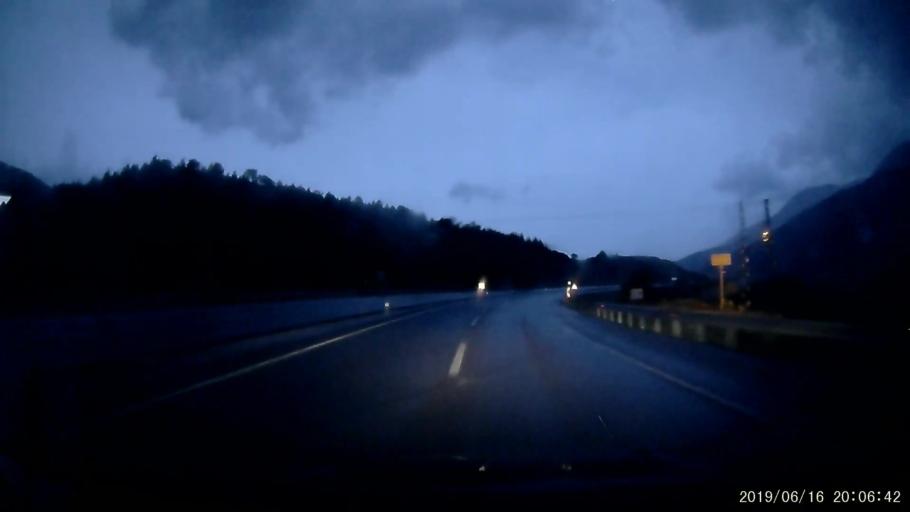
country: TR
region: Sivas
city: Dogansar
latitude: 40.3152
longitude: 37.6360
